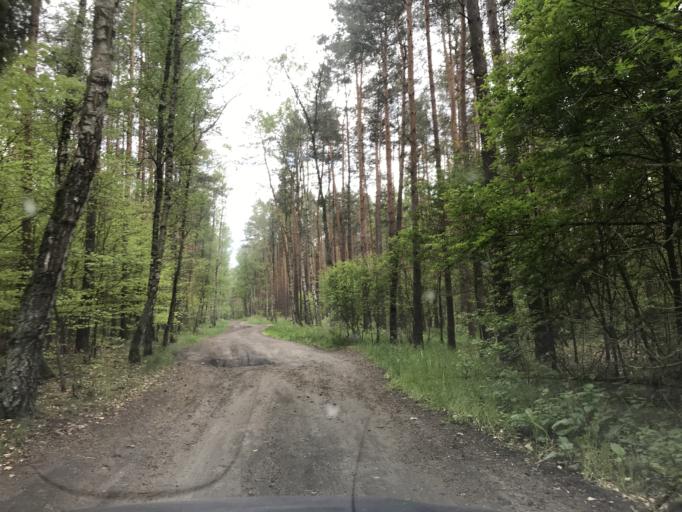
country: PL
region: West Pomeranian Voivodeship
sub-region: Powiat mysliborski
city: Mysliborz
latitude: 52.8688
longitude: 14.8844
